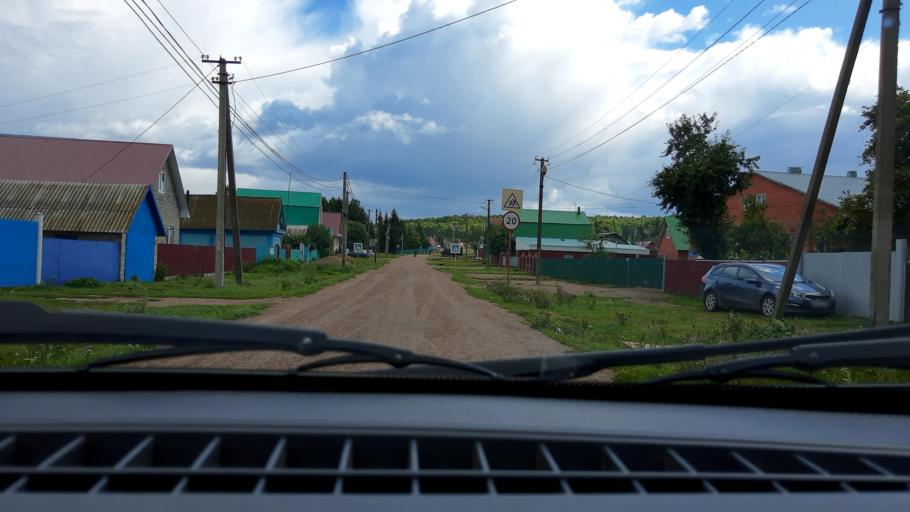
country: RU
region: Bashkortostan
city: Blagoveshchensk
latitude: 54.9479
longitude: 55.8686
